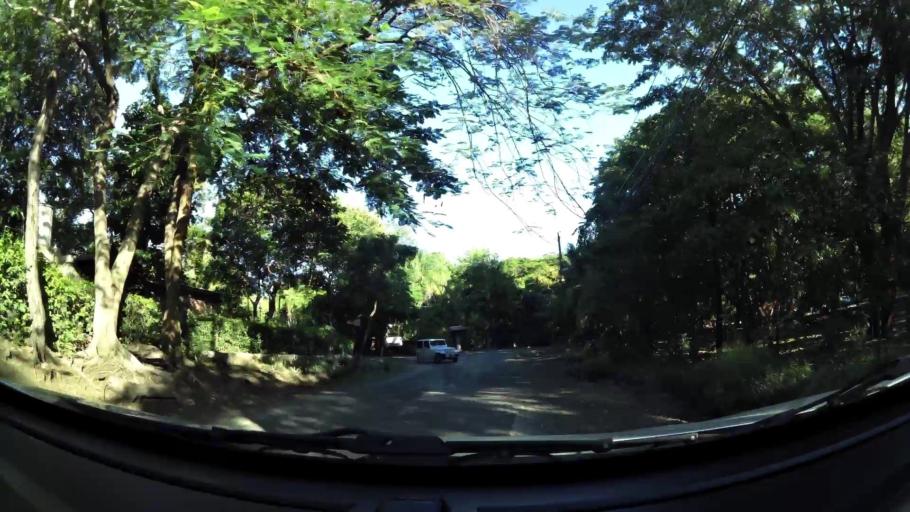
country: CR
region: Guanacaste
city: Sardinal
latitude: 10.5704
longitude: -85.6807
